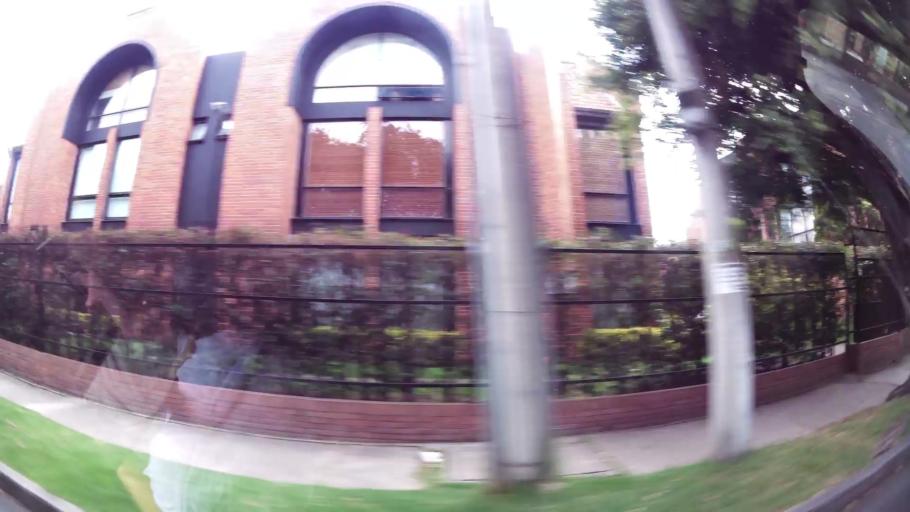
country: CO
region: Bogota D.C.
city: Barrio San Luis
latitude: 4.7193
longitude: -74.0320
